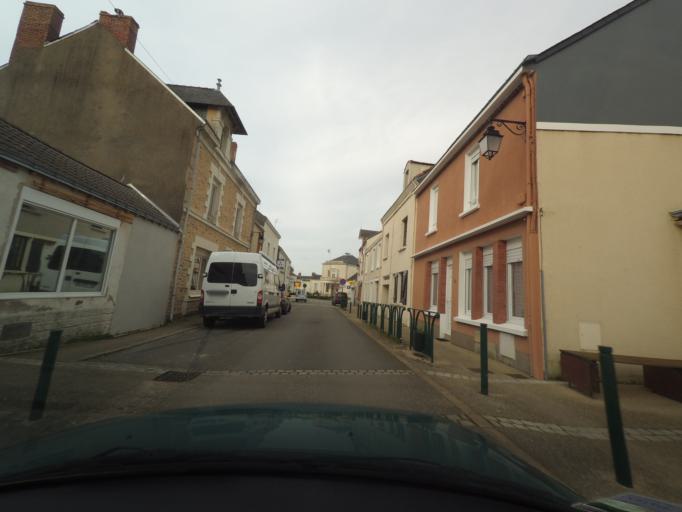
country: FR
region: Pays de la Loire
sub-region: Departement de la Loire-Atlantique
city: Saint-Pere-en-Retz
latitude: 47.2069
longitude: -2.0441
